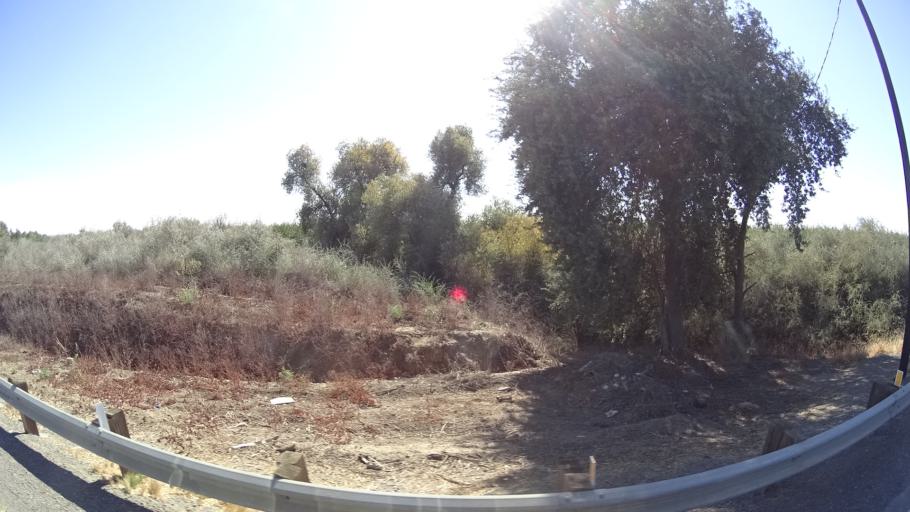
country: US
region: California
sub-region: Yolo County
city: Woodland
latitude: 38.6196
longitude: -121.8319
